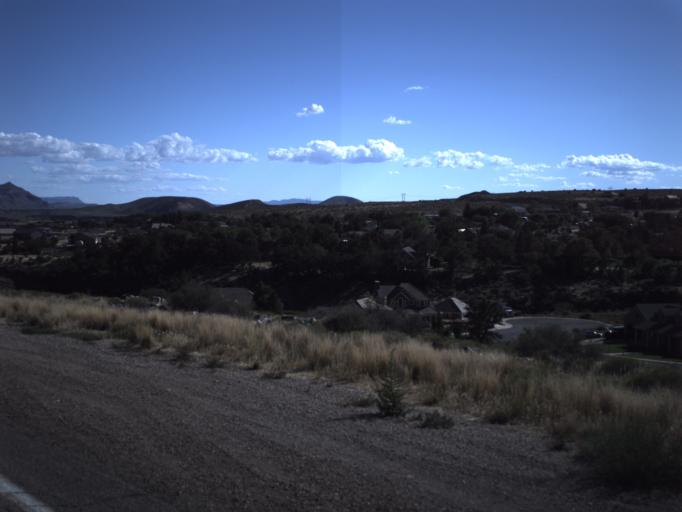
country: US
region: Utah
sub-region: Washington County
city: Toquerville
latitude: 37.2455
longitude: -113.2837
